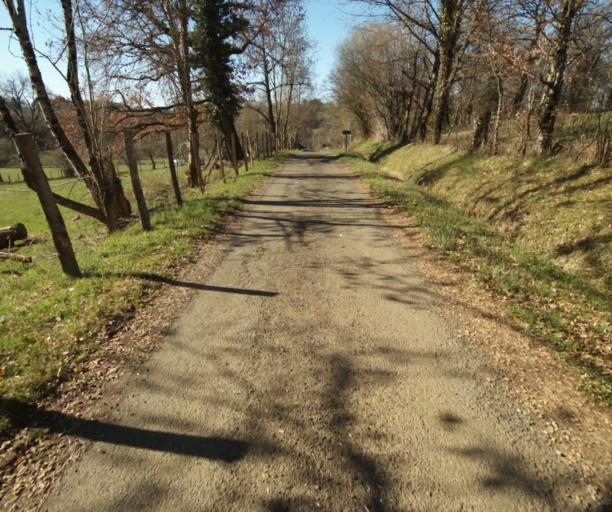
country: FR
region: Limousin
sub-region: Departement de la Correze
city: Chamboulive
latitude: 45.4021
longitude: 1.7038
